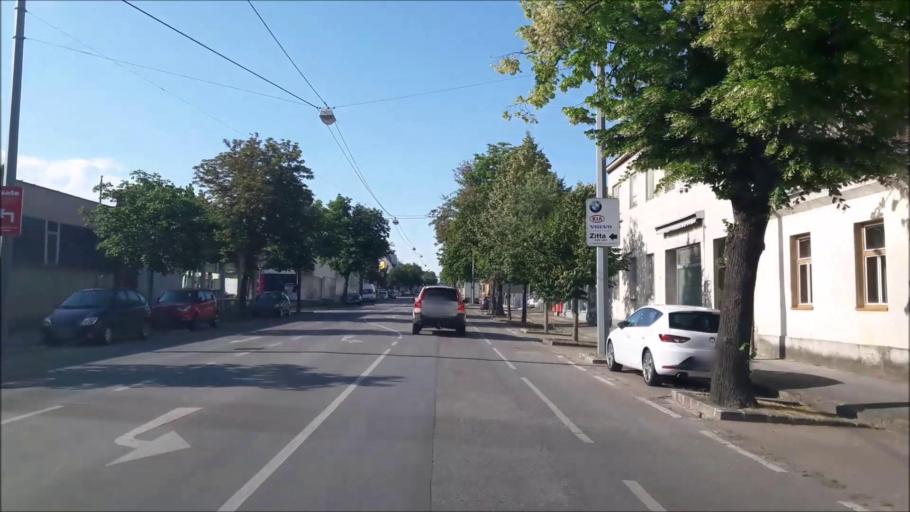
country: AT
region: Lower Austria
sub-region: Politischer Bezirk Wien-Umgebung
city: Leopoldsdorf
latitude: 48.1402
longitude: 16.3829
